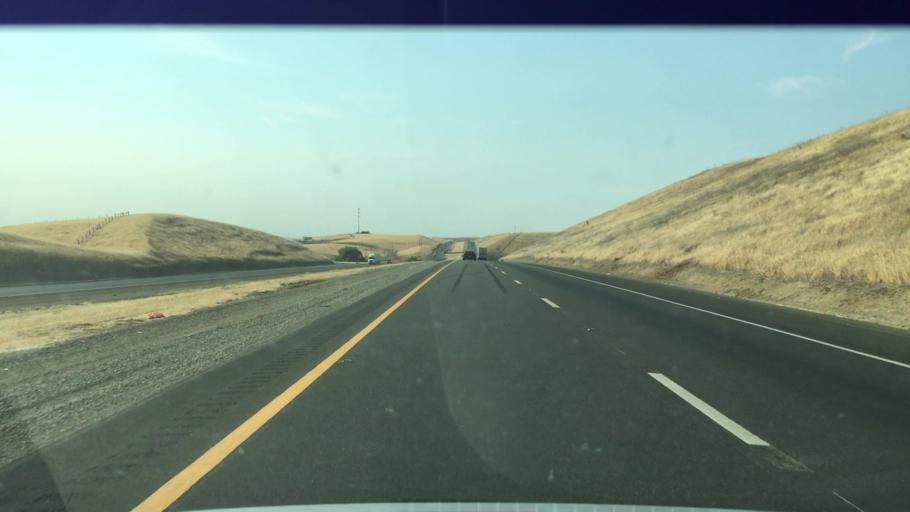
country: US
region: California
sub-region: Stanislaus County
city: Patterson
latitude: 37.4283
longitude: -121.1575
